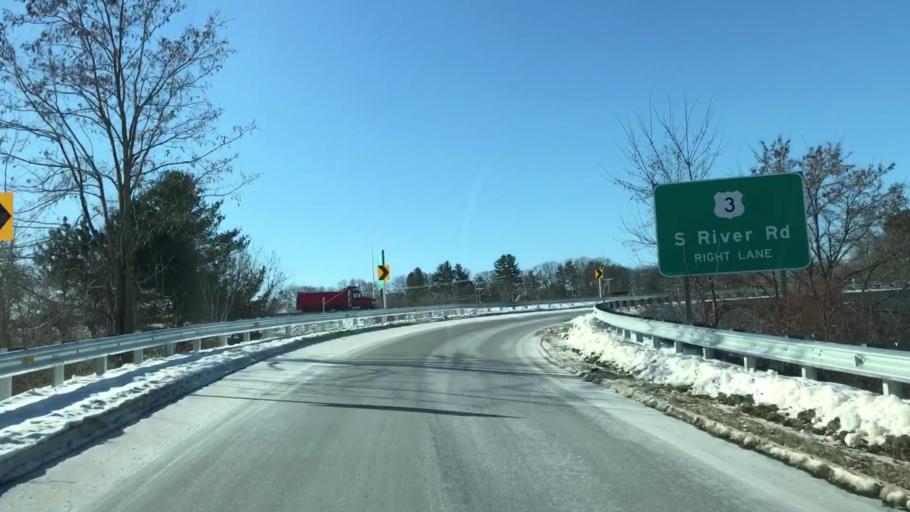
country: US
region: New Hampshire
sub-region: Hillsborough County
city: Bedford
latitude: 42.9513
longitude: -71.4756
